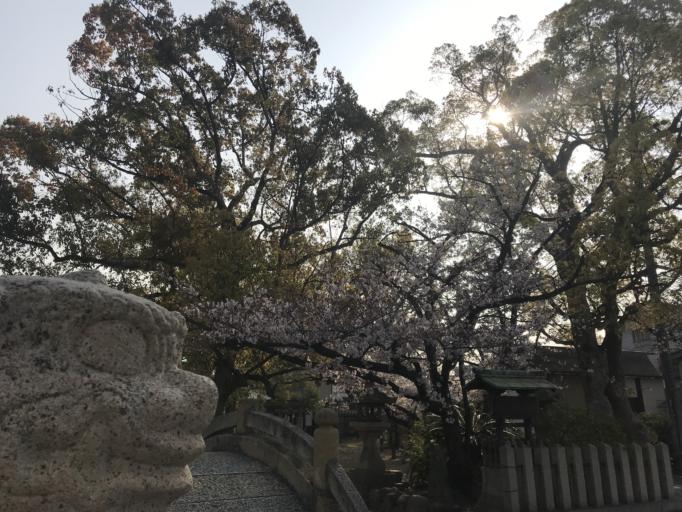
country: JP
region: Osaka
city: Izumi
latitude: 34.4961
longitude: 135.4192
